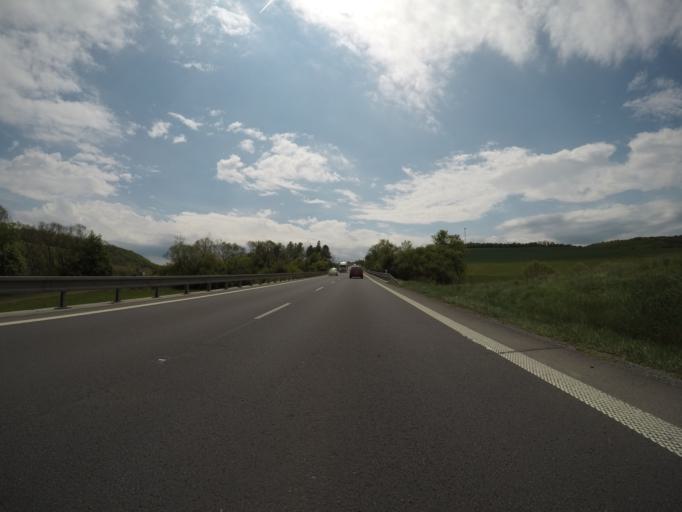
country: SK
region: Banskobystricky
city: Krupina
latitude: 48.4570
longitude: 19.0967
